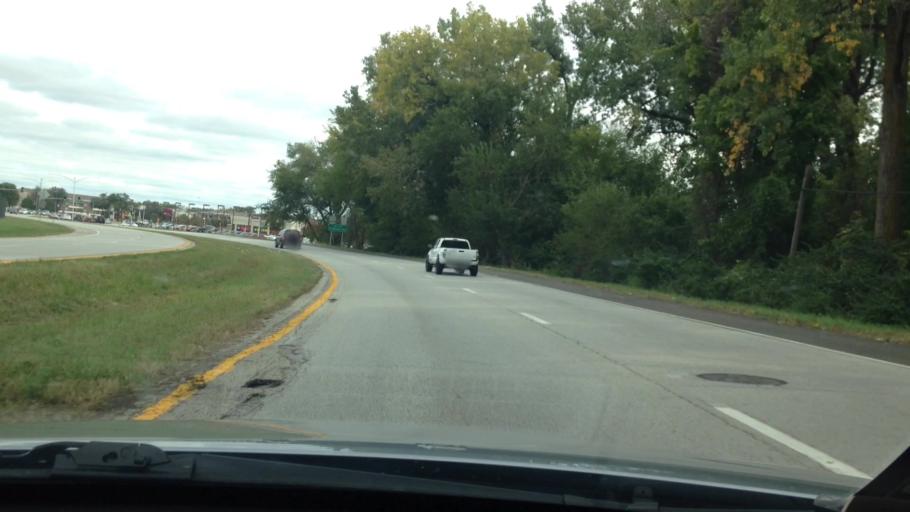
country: US
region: Missouri
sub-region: Clay County
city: North Kansas City
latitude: 39.1533
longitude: -94.5846
